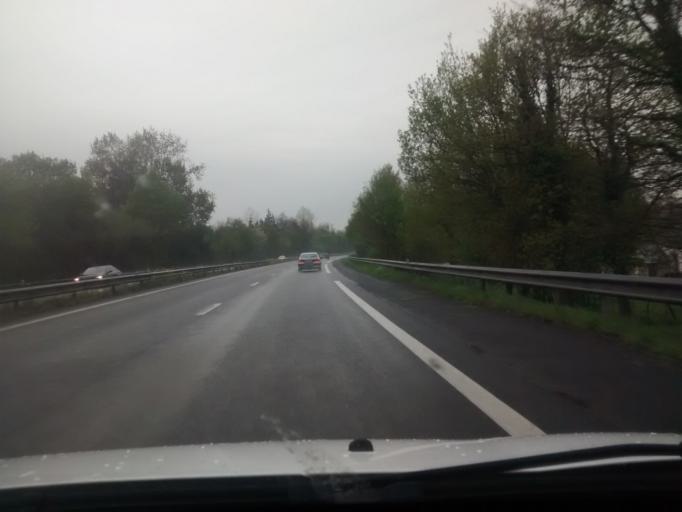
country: FR
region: Brittany
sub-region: Departement des Cotes-d'Armor
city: Broons
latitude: 48.2988
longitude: -2.2307
